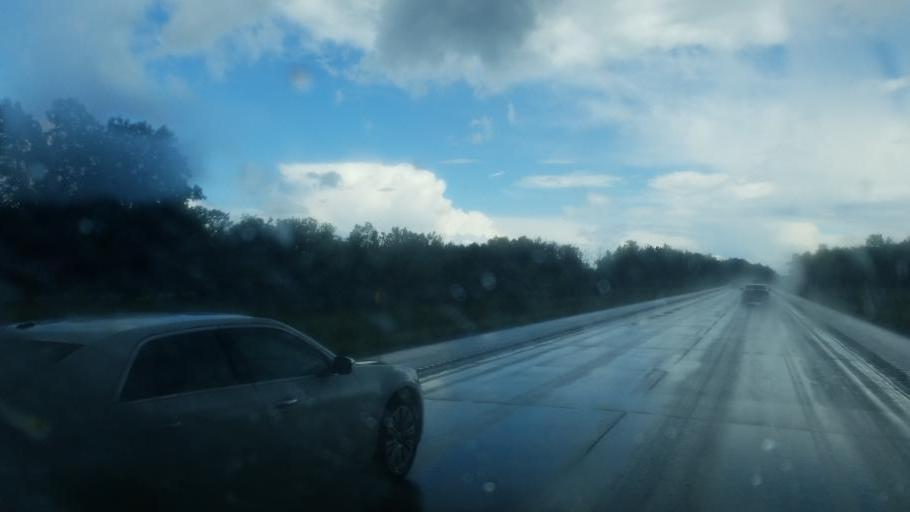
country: US
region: New York
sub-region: Erie County
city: Eden
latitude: 42.6819
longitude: -78.9409
